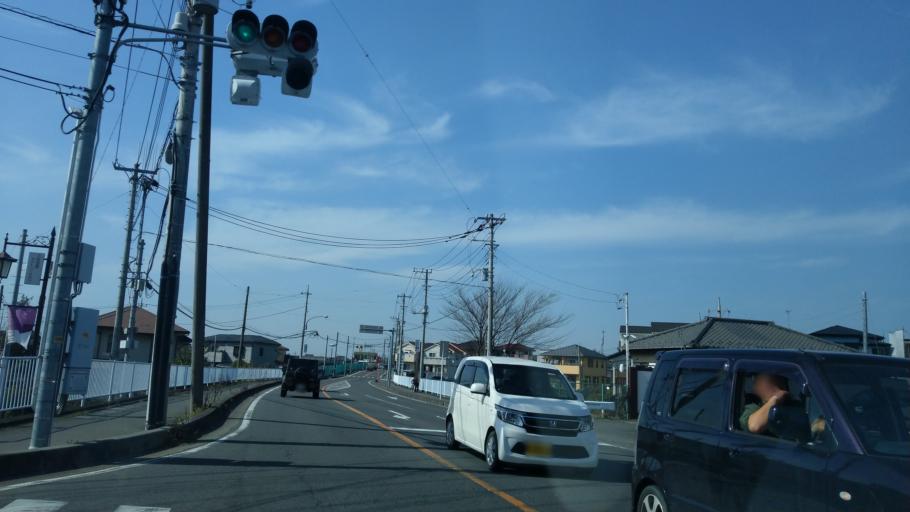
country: JP
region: Saitama
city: Ageoshimo
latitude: 35.9231
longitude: 139.5624
